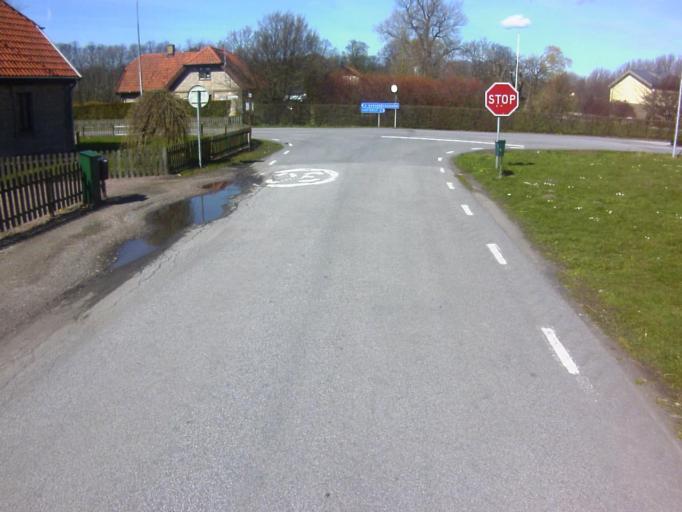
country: SE
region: Skane
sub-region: Kavlinge Kommun
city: Hofterup
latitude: 55.7735
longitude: 12.9543
